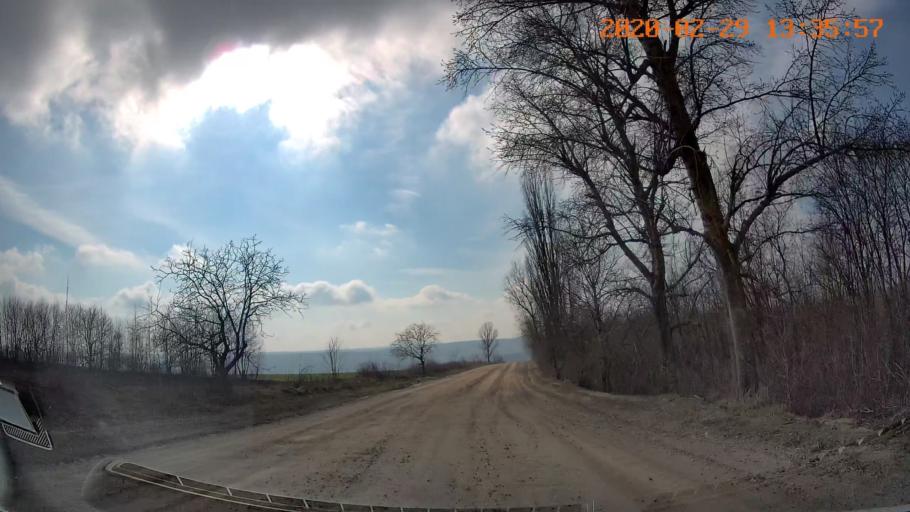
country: MD
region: Telenesti
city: Camenca
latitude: 47.8636
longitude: 28.6096
